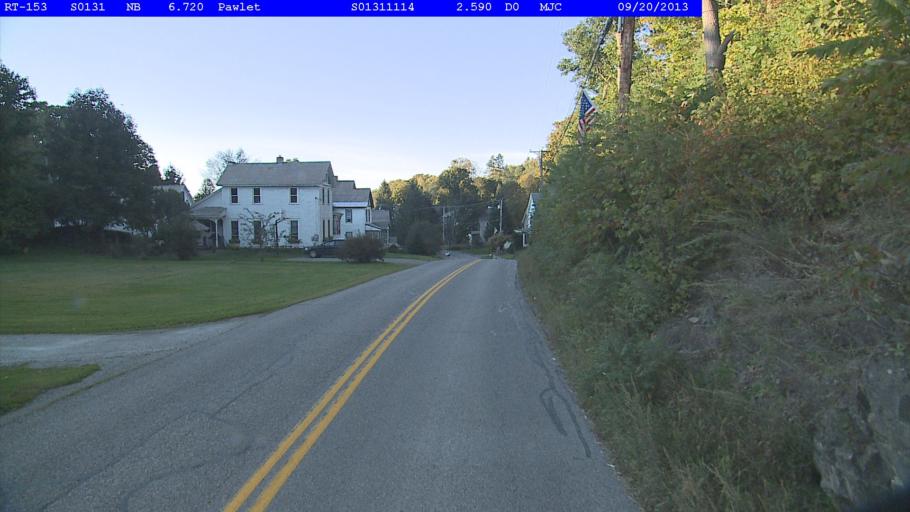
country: US
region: New York
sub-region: Washington County
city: Granville
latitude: 43.3503
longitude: -73.2495
